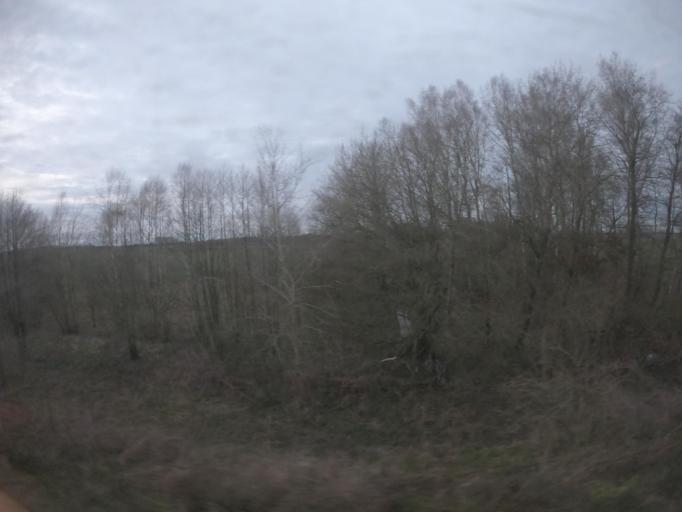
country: PL
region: West Pomeranian Voivodeship
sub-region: Powiat szczecinecki
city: Lubowo
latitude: 53.5662
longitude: 16.3501
